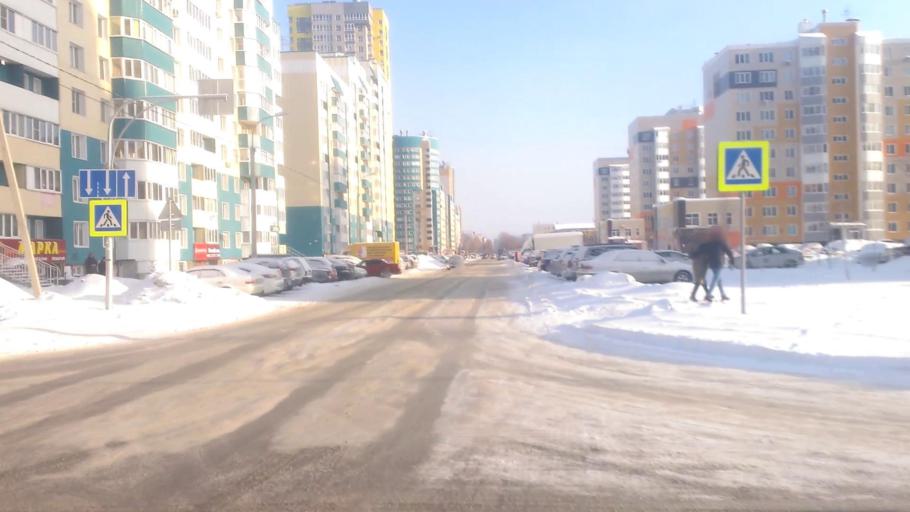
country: RU
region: Altai Krai
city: Novosilikatnyy
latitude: 53.3409
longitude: 83.6547
